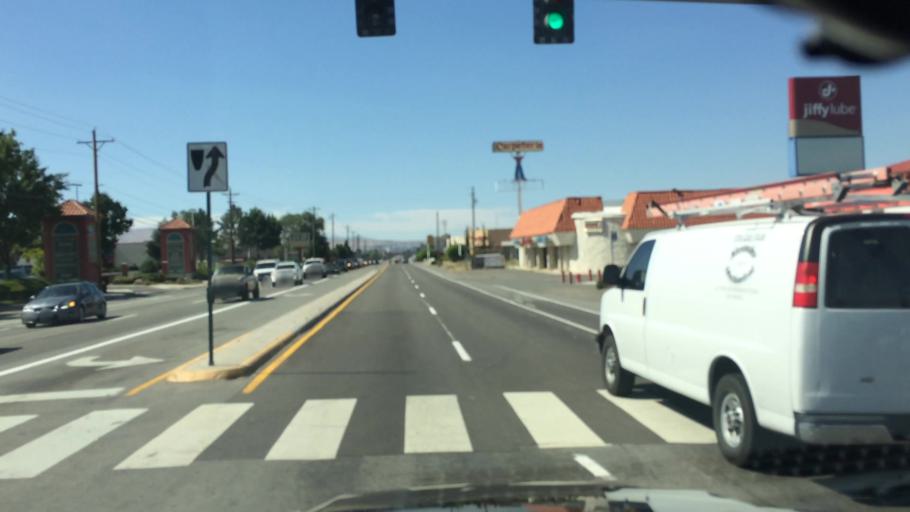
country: US
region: Nevada
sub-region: Washoe County
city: Reno
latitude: 39.4525
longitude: -119.7772
